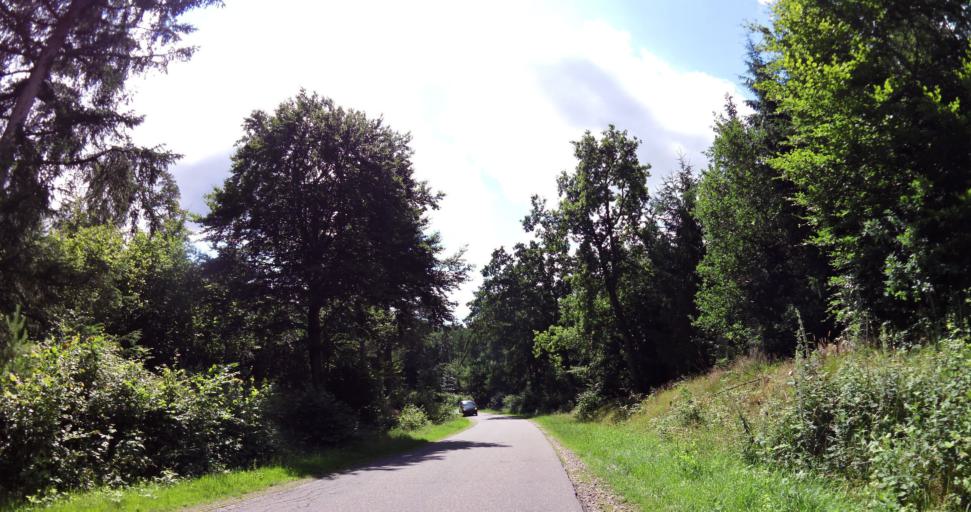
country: DE
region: Schleswig-Holstein
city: Brodersby
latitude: 54.5110
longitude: 9.7196
